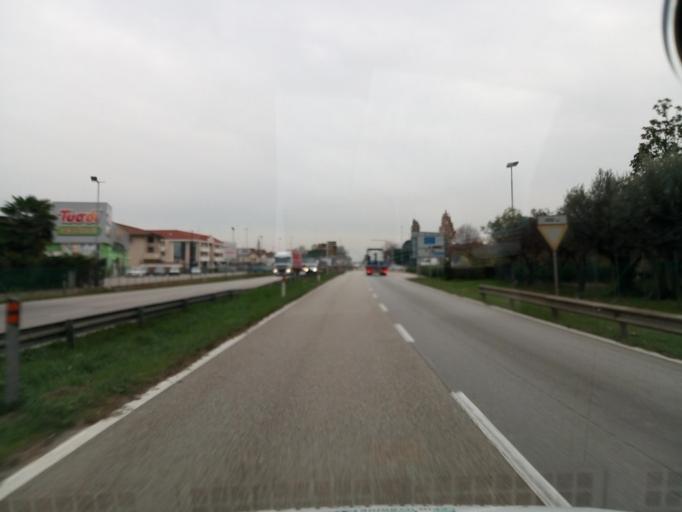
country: IT
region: Veneto
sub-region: Provincia di Padova
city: Villatora
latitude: 45.3871
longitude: 11.9597
